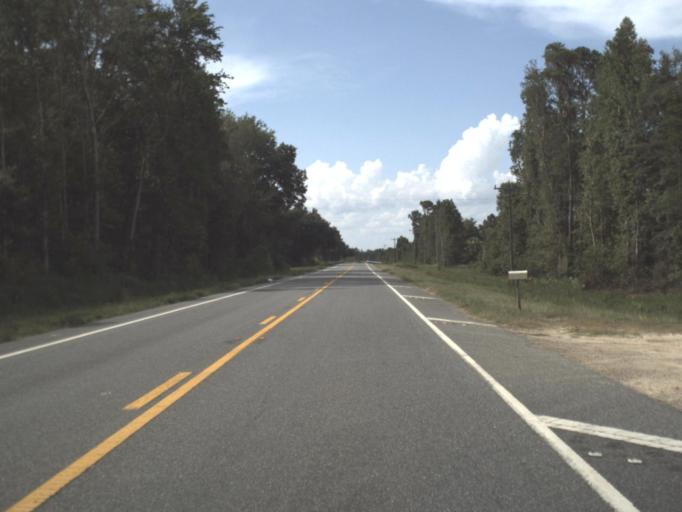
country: US
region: Florida
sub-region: Taylor County
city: Perry
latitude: 30.1968
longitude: -83.6053
